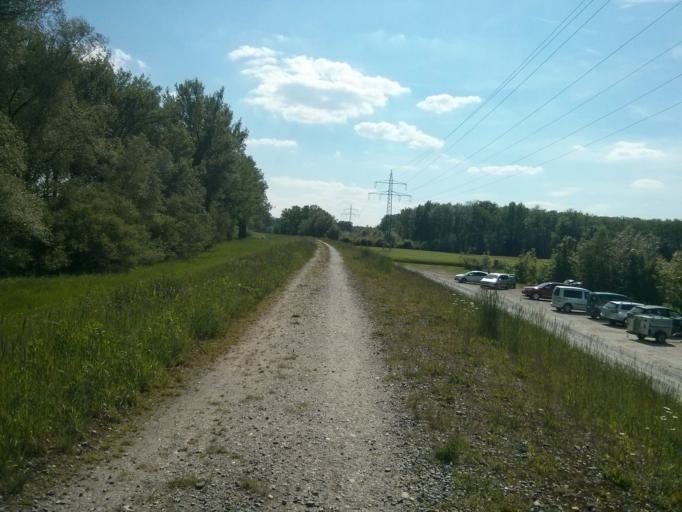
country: DE
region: Bavaria
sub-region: Lower Bavaria
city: Plattling
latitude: 48.7682
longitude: 12.8741
